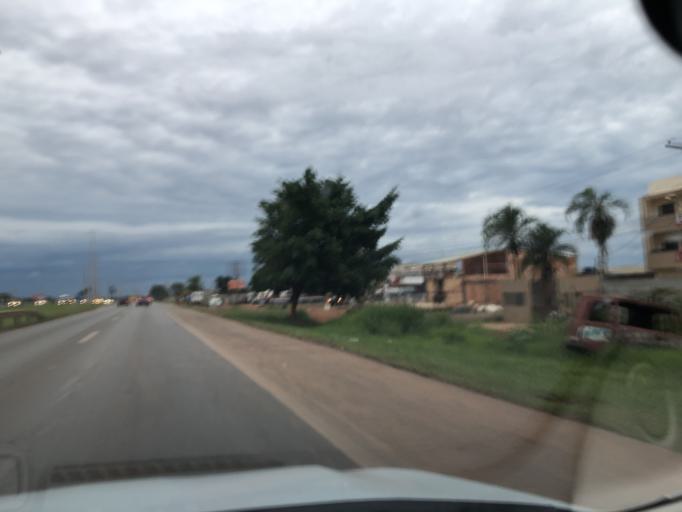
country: BR
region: Goias
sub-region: Luziania
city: Luziania
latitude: -16.1386
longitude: -47.9510
